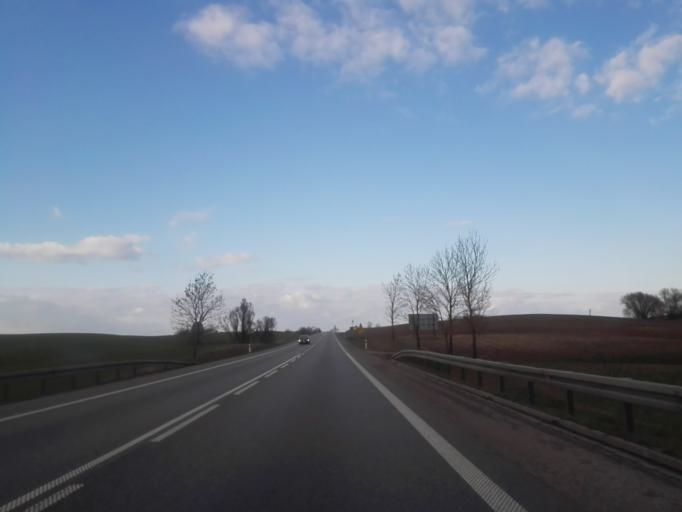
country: PL
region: Podlasie
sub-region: Suwalki
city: Suwalki
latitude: 54.2048
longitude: 23.0236
